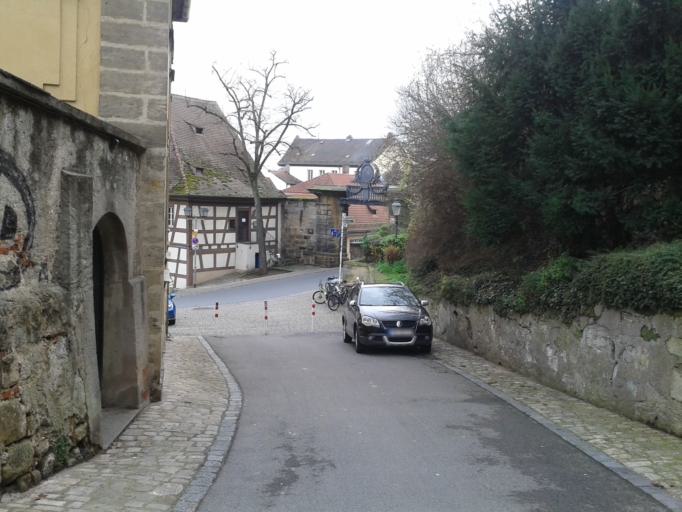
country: DE
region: Bavaria
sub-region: Upper Franconia
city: Bamberg
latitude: 49.8923
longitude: 10.8816
